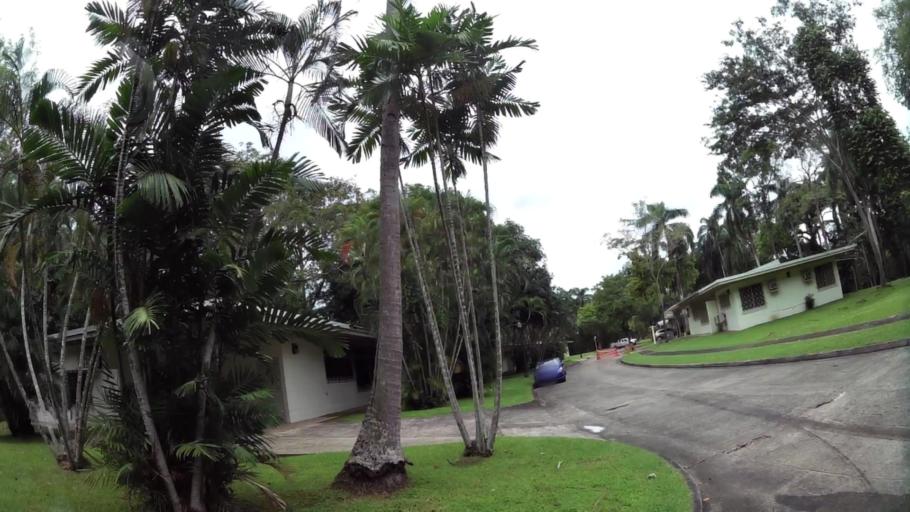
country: PA
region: Panama
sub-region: Distrito de Panama
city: Ancon
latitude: 8.9582
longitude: -79.5526
